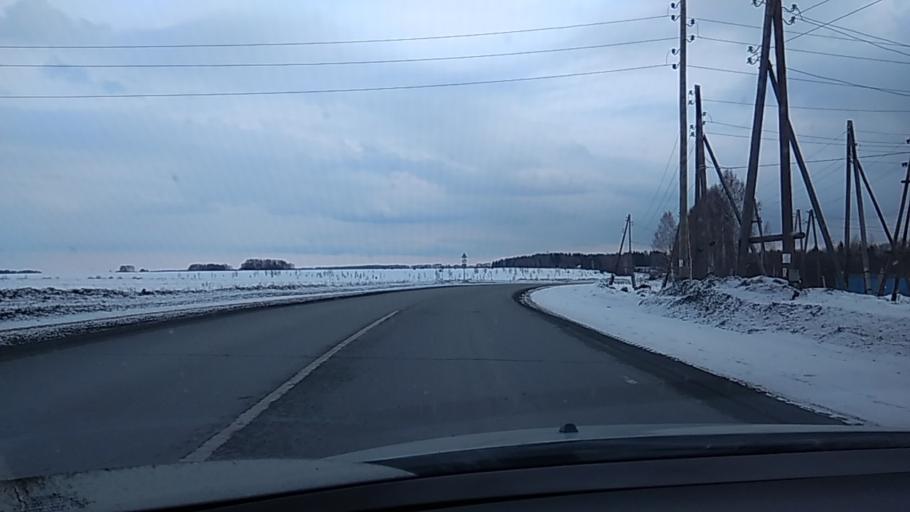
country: RU
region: Sverdlovsk
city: Sovkhoznyy
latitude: 56.6103
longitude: 61.2996
